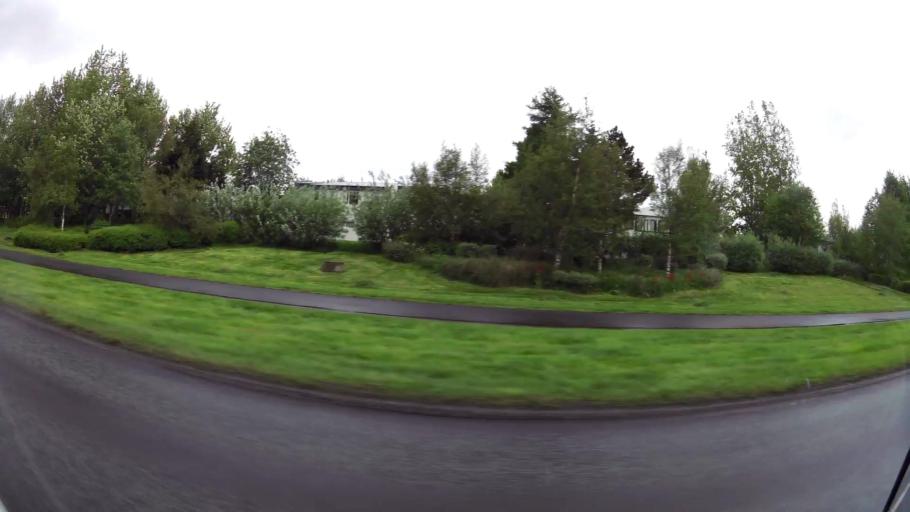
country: IS
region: Northeast
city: Akureyri
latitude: 65.6880
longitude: -18.1294
